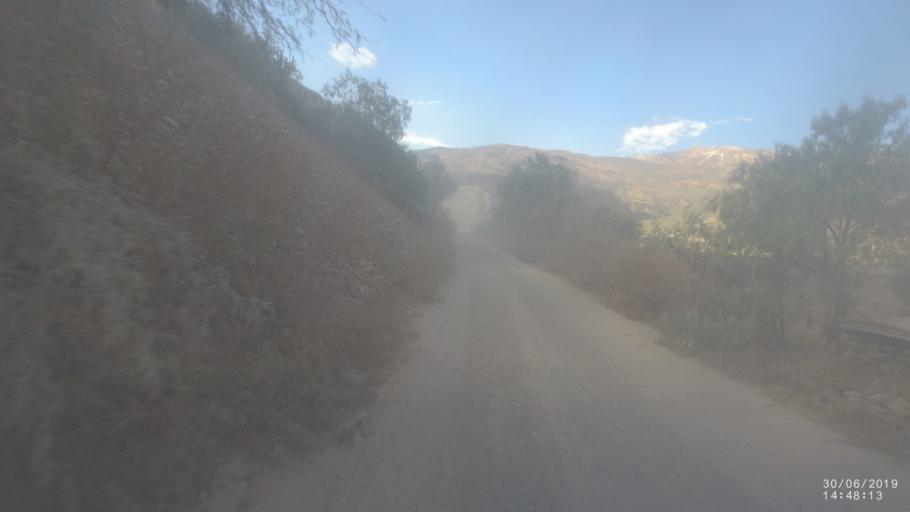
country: BO
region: Cochabamba
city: Irpa Irpa
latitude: -17.7902
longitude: -66.3440
